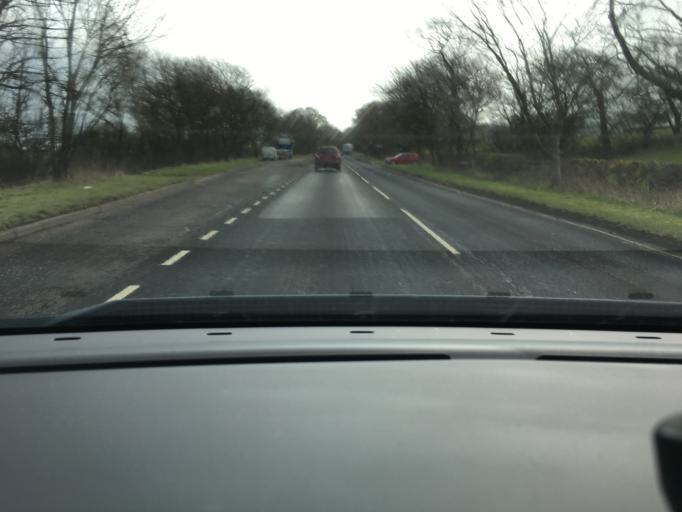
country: GB
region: Scotland
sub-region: West Lothian
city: Linlithgow
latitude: 56.0037
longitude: -3.5694
